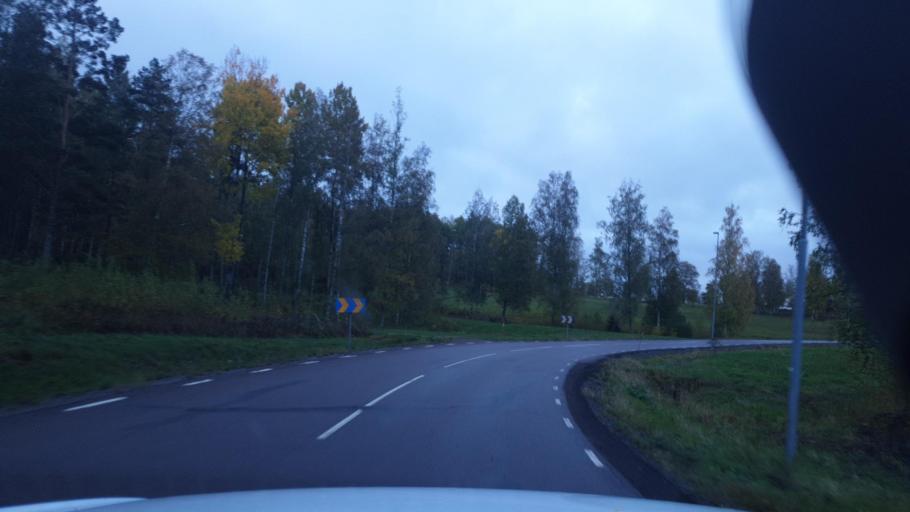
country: SE
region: Vaermland
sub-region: Arvika Kommun
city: Arvika
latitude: 59.7828
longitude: 12.6208
